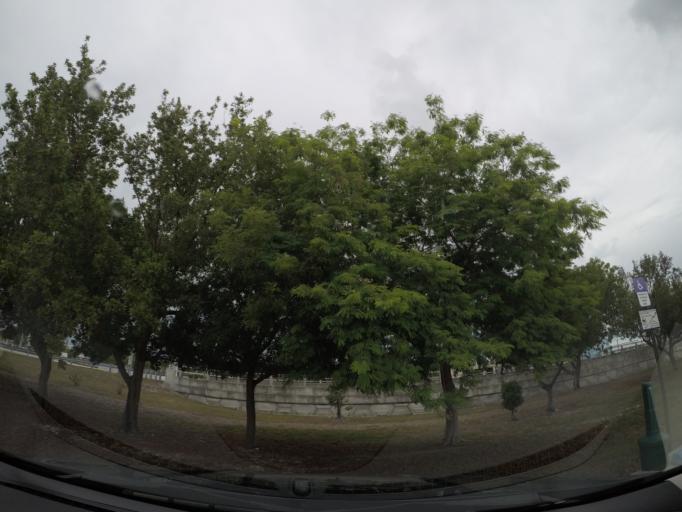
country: US
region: Florida
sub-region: Monroe County
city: Tavernier
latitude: 25.0030
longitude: -80.5339
